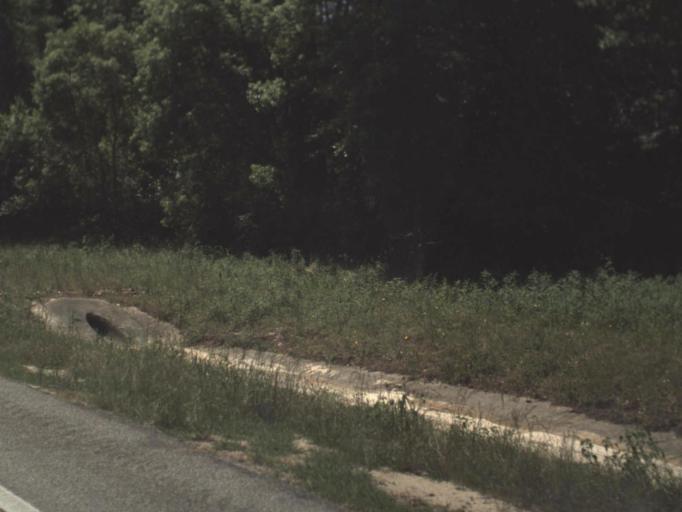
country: US
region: Florida
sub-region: Jackson County
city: Marianna
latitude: 30.6513
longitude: -85.2107
